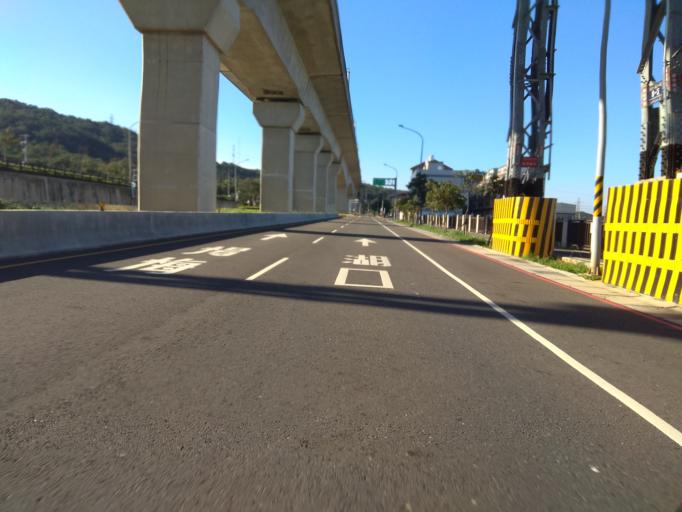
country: TW
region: Taiwan
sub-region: Hsinchu
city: Zhubei
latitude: 24.8825
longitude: 121.0697
